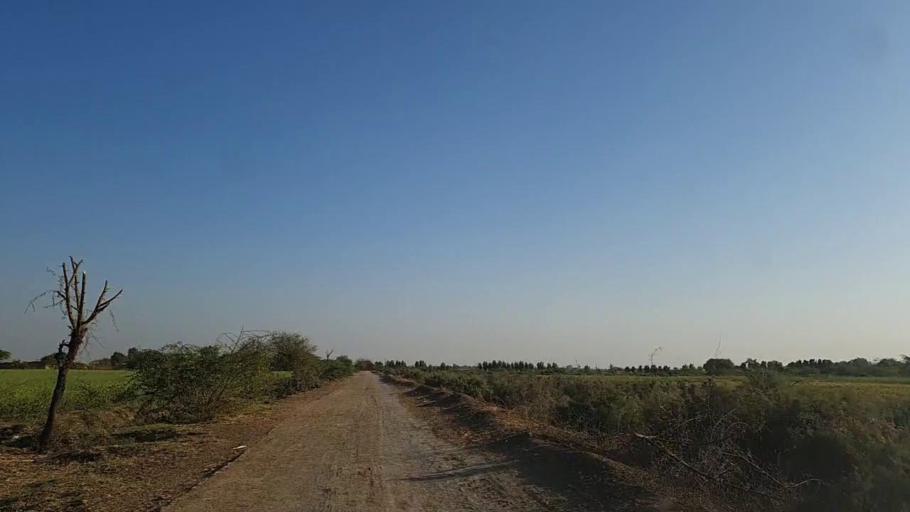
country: PK
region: Sindh
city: Samaro
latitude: 25.3340
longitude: 69.4119
